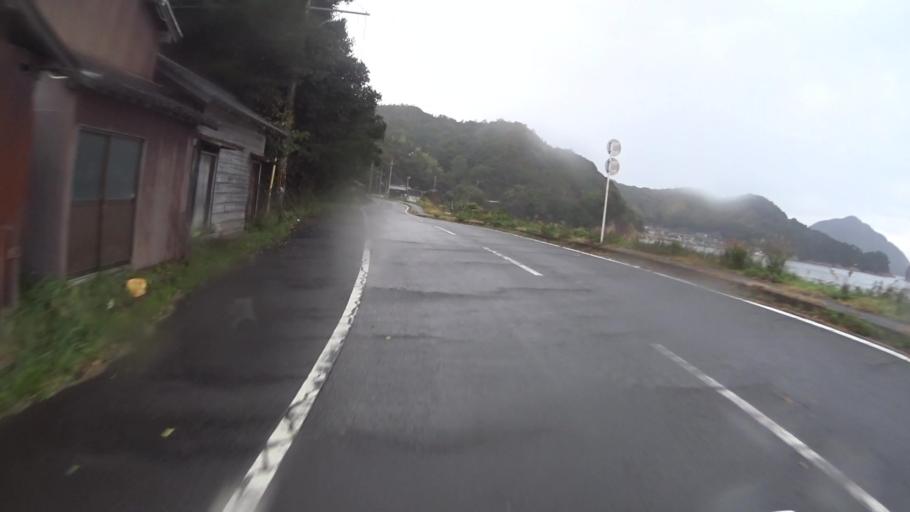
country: JP
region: Kyoto
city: Miyazu
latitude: 35.5686
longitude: 135.2526
